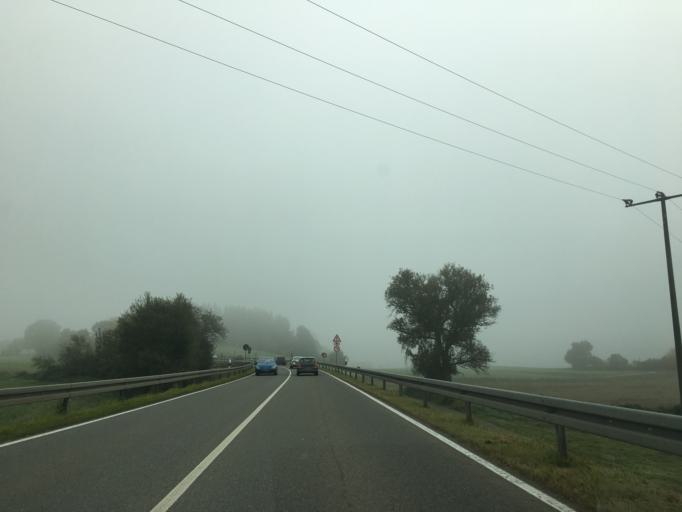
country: CH
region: Thurgau
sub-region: Kreuzlingen District
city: Gottlieben
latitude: 47.7005
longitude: 9.1274
